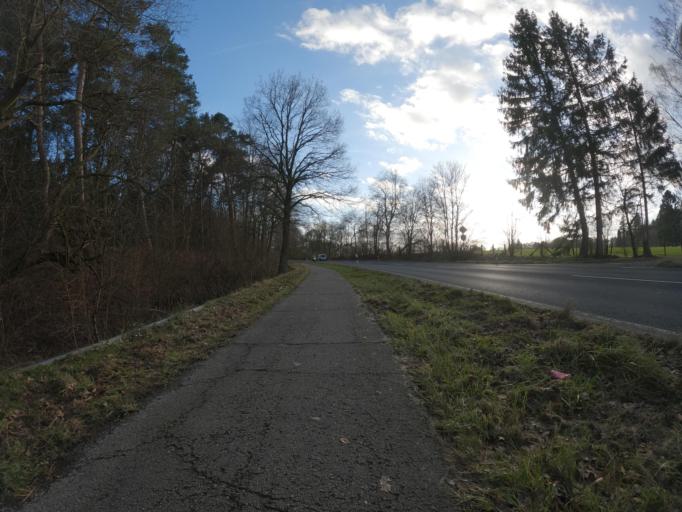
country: DE
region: North Rhine-Westphalia
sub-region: Regierungsbezirk Koln
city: Aachen
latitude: 50.7282
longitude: 6.0894
